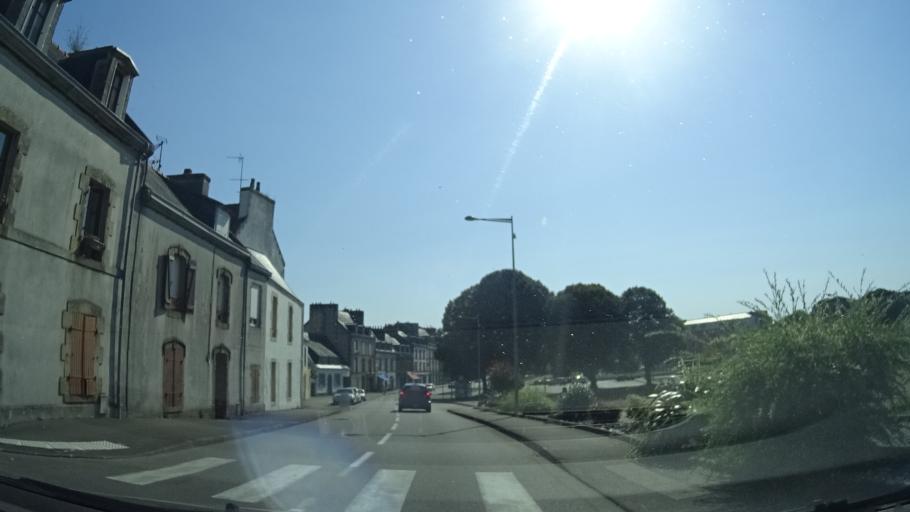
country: FR
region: Brittany
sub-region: Departement du Finistere
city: Douarnenez
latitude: 48.0926
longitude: -4.3373
